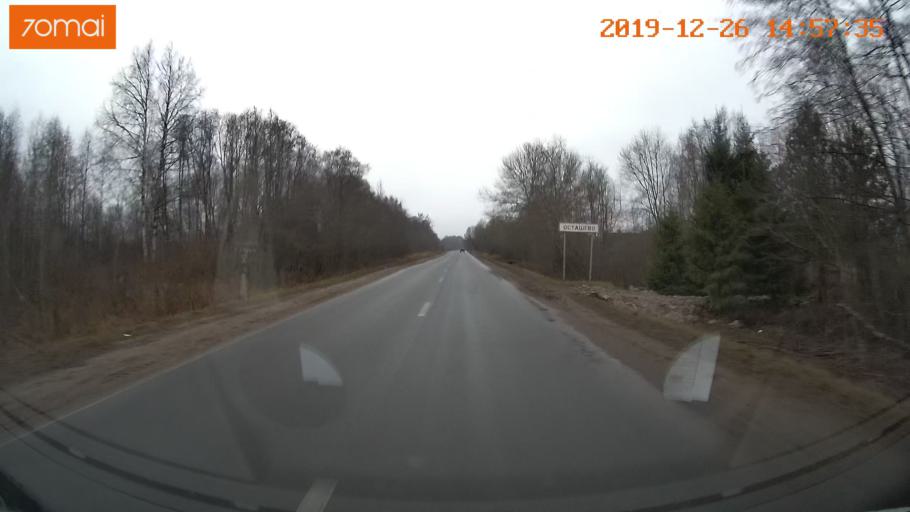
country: RU
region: Jaroslavl
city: Rybinsk
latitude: 58.2810
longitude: 38.8618
